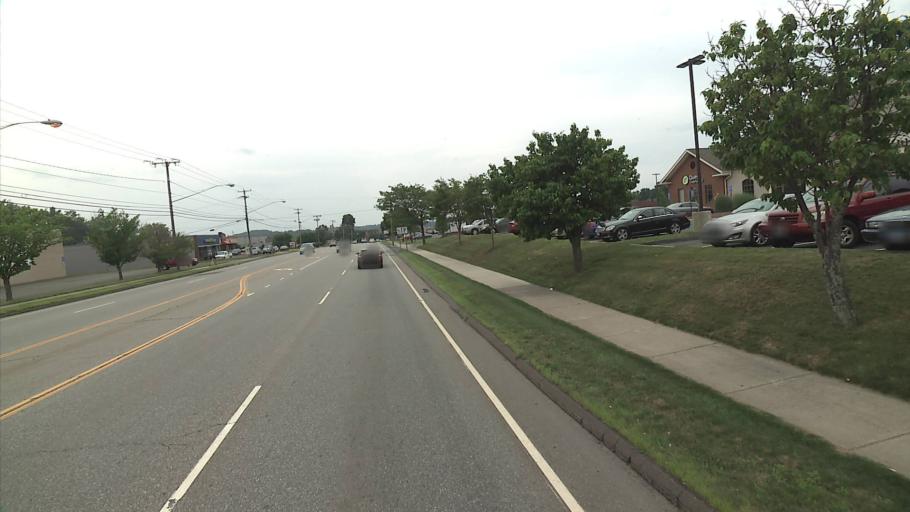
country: US
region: Connecticut
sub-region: Hartford County
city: Wethersfield
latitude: 41.6955
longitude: -72.6574
